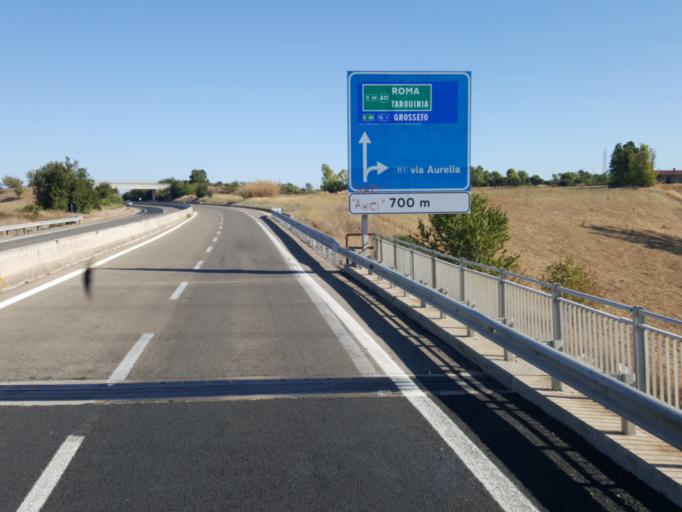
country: IT
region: Latium
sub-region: Citta metropolitana di Roma Capitale
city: Aurelia
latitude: 42.1511
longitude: 11.7918
